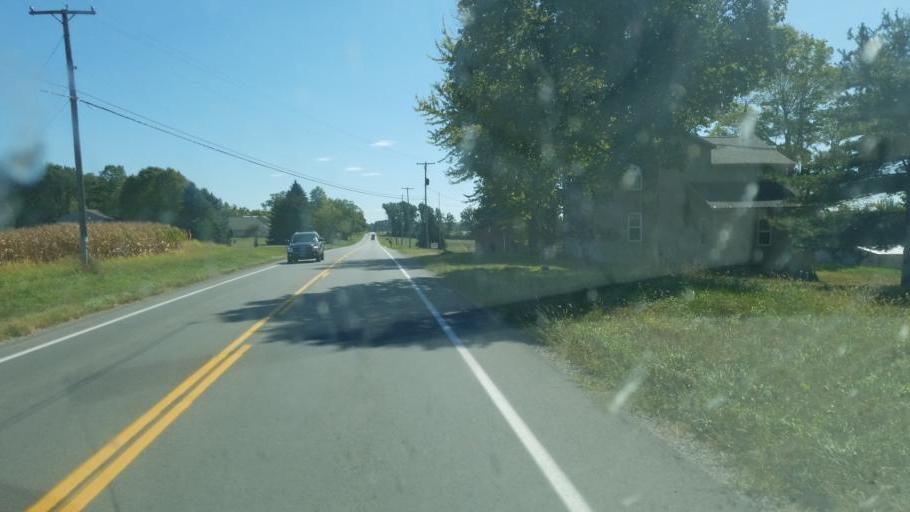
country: US
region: Ohio
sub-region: Huron County
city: Plymouth
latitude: 41.0211
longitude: -82.6778
